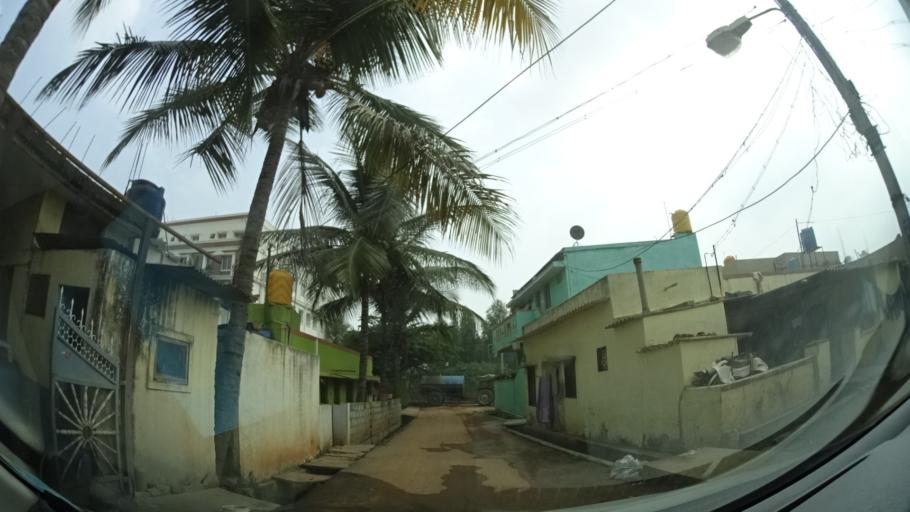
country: IN
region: Karnataka
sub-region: Bangalore Rural
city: Hoskote
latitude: 12.9811
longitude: 77.7560
